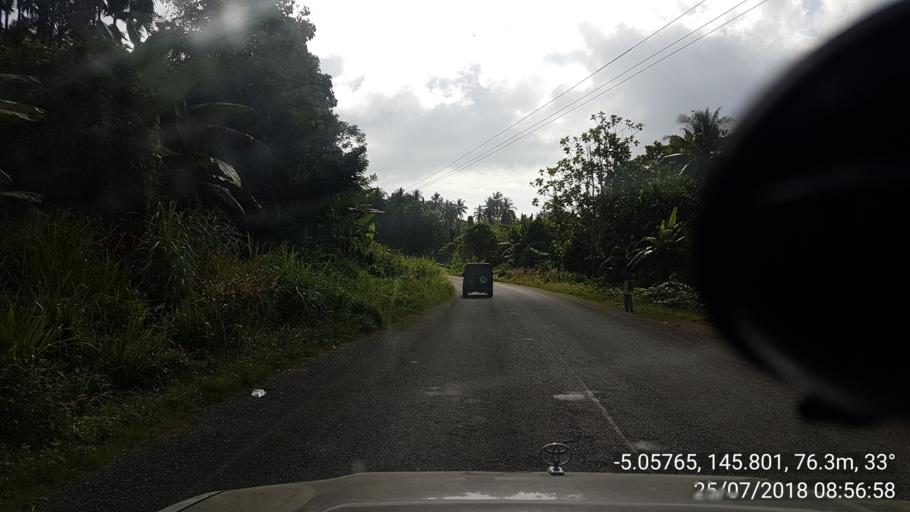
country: PG
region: Madang
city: Madang
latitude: -5.0578
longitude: 145.8008
